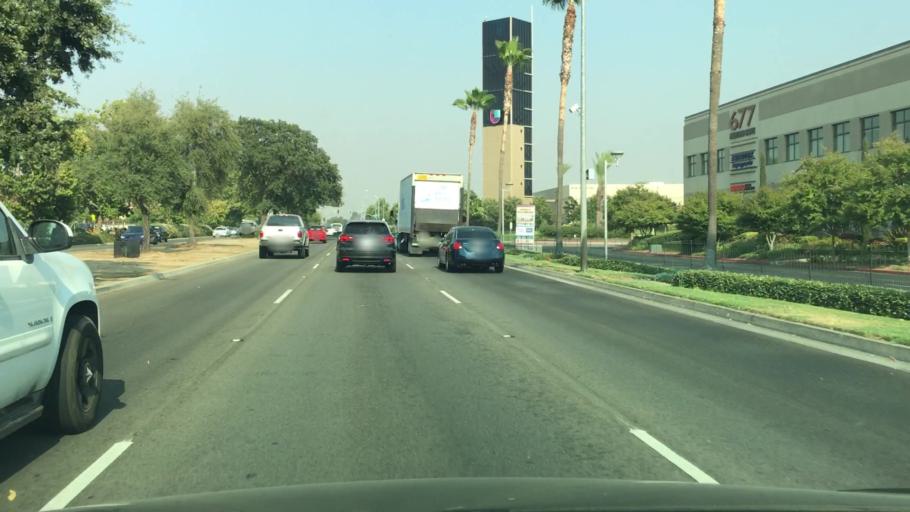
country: US
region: California
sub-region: Fresno County
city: Fresno
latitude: 36.8369
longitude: -119.8054
